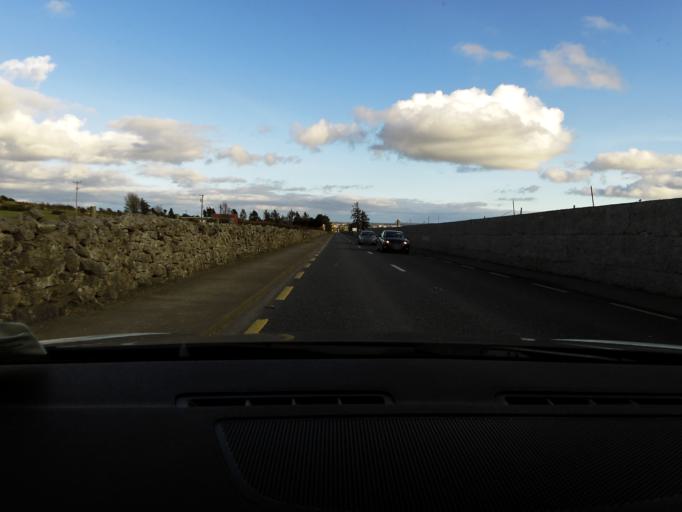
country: IE
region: Connaught
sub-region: Roscommon
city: Roscommon
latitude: 53.6469
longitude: -8.2222
